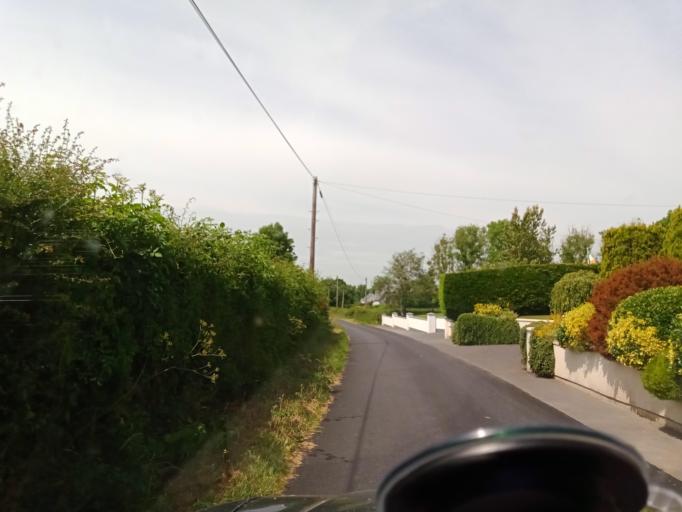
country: IE
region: Leinster
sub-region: Kilkenny
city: Thomastown
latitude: 52.5559
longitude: -7.1099
